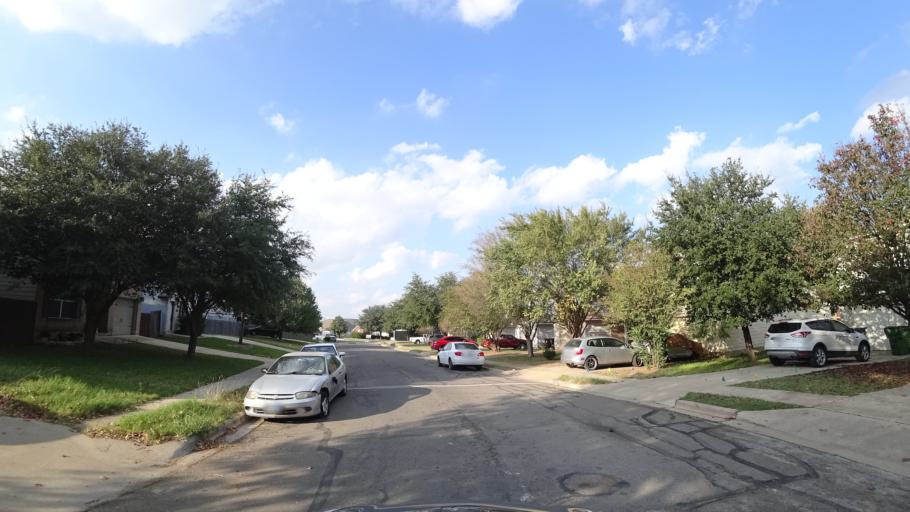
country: US
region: Texas
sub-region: Williamson County
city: Round Rock
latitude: 30.4898
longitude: -97.6586
